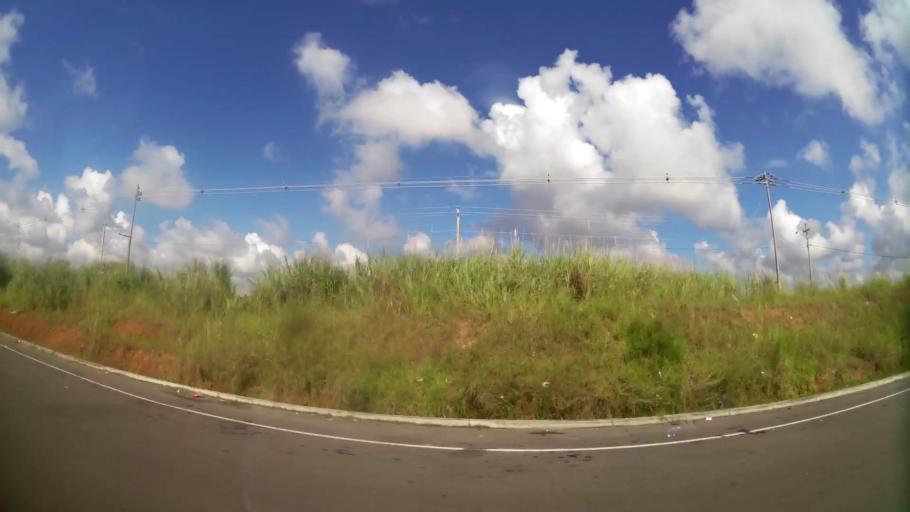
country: PA
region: Panama
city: Nuevo Arraijan
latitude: 8.8982
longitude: -79.7436
